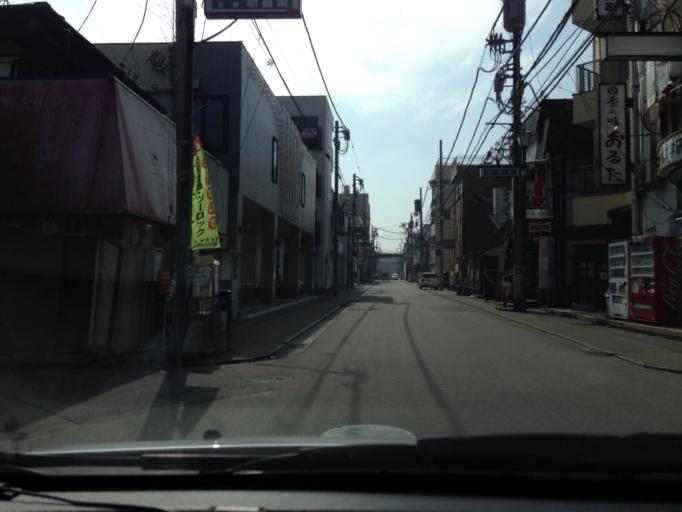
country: JP
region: Ibaraki
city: Naka
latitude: 36.0773
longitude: 140.2011
